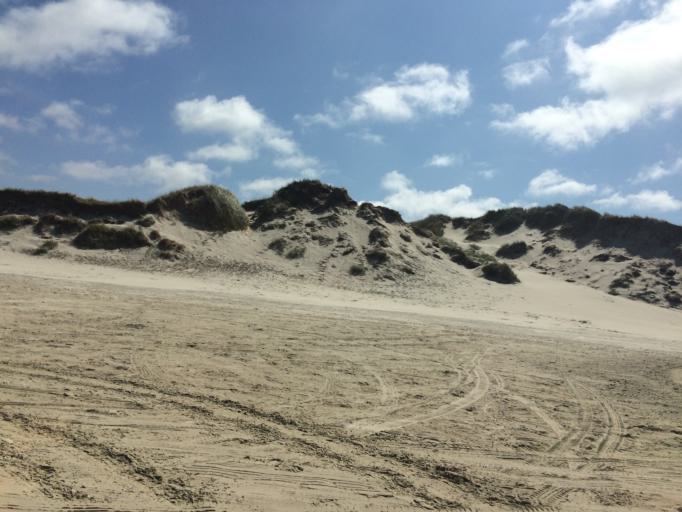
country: DK
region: North Denmark
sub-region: Jammerbugt Kommune
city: Pandrup
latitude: 57.2490
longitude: 9.5717
